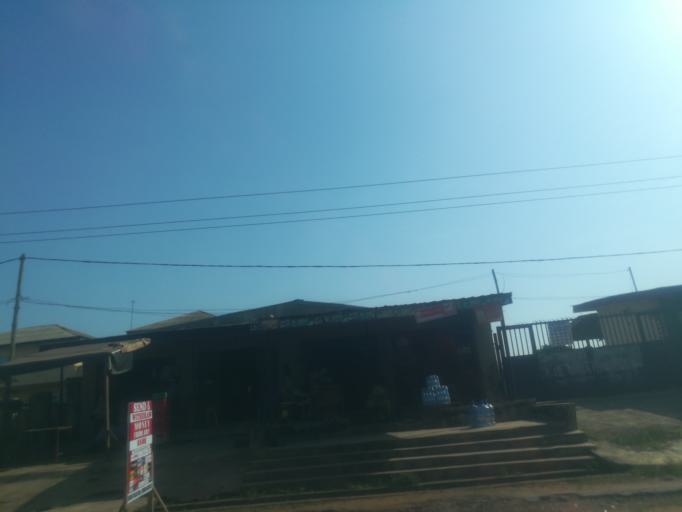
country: NG
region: Ogun
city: Abeokuta
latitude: 7.1368
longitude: 3.2916
